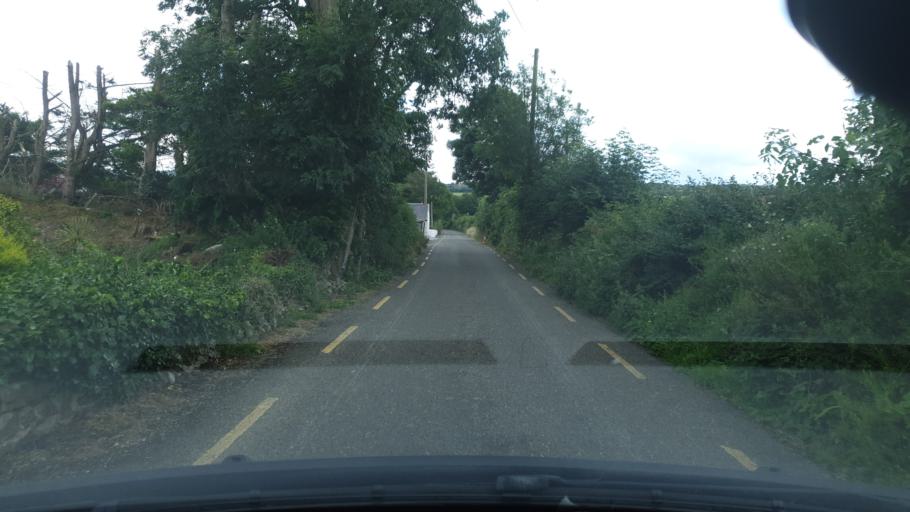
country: IE
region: Munster
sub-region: Ciarrai
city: Tralee
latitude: 52.2497
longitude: -9.6456
